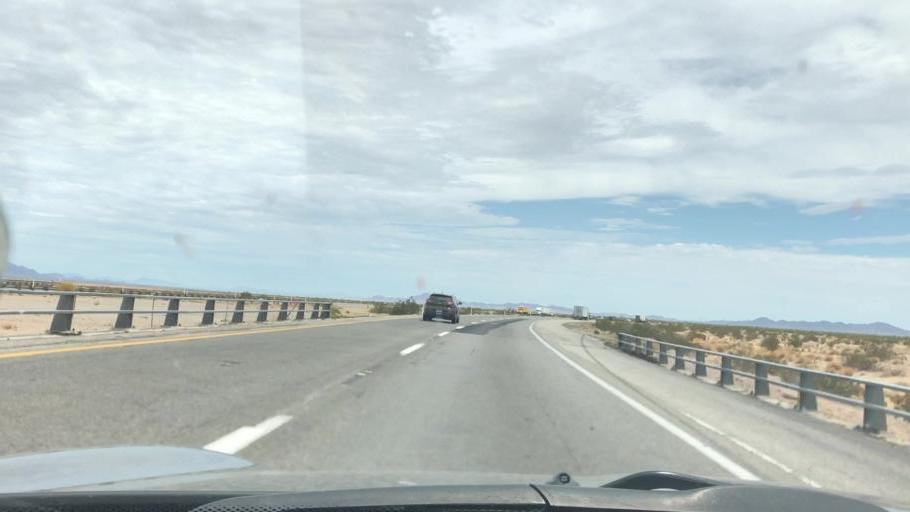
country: US
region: California
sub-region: Riverside County
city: Mesa Verde
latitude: 33.6356
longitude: -115.0820
